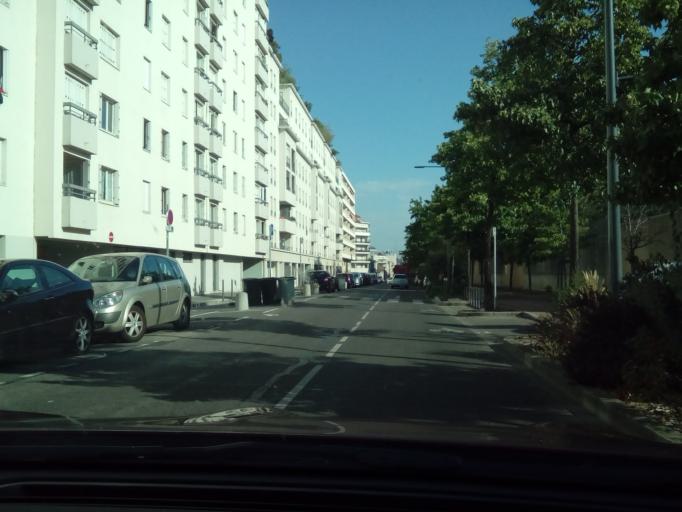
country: FR
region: Rhone-Alpes
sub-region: Departement du Rhone
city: Villeurbanne
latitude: 45.7564
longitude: 4.8854
